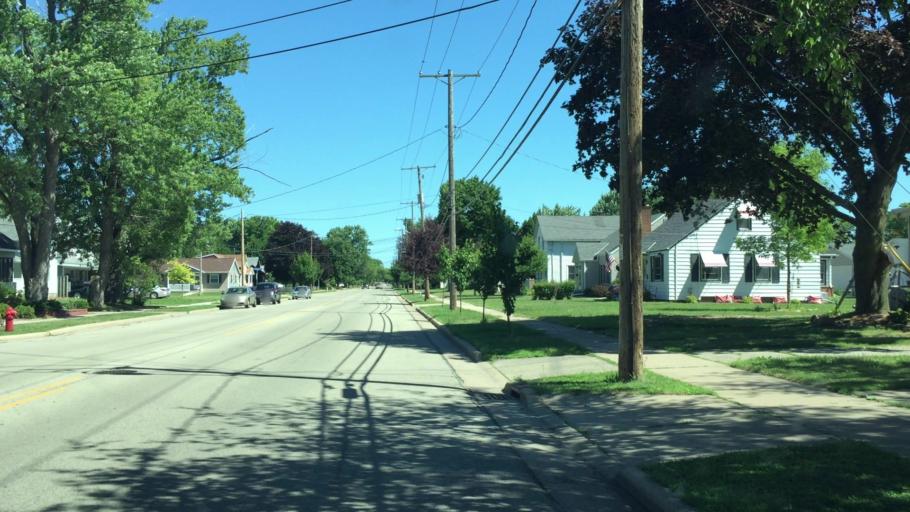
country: US
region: Wisconsin
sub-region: Winnebago County
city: Menasha
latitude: 44.2089
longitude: -88.4531
